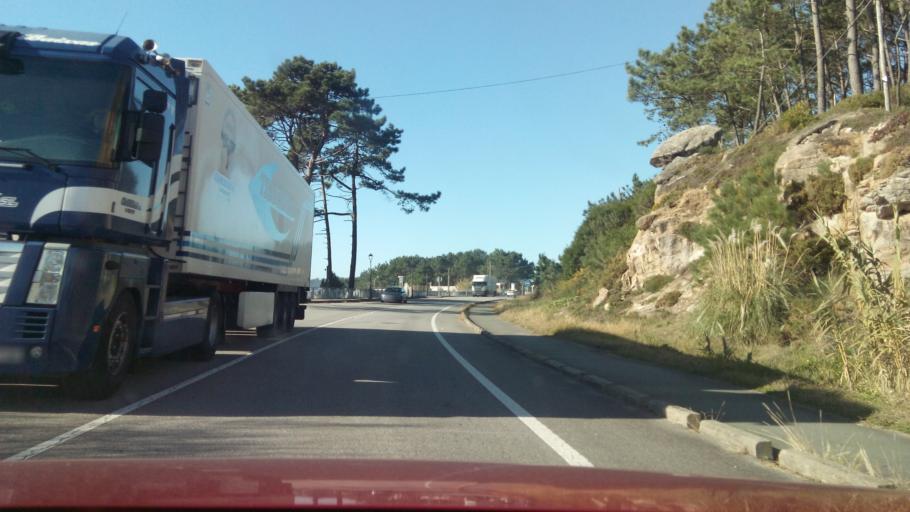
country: ES
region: Galicia
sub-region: Provincia de Pontevedra
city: O Grove
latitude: 42.4585
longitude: -8.8888
